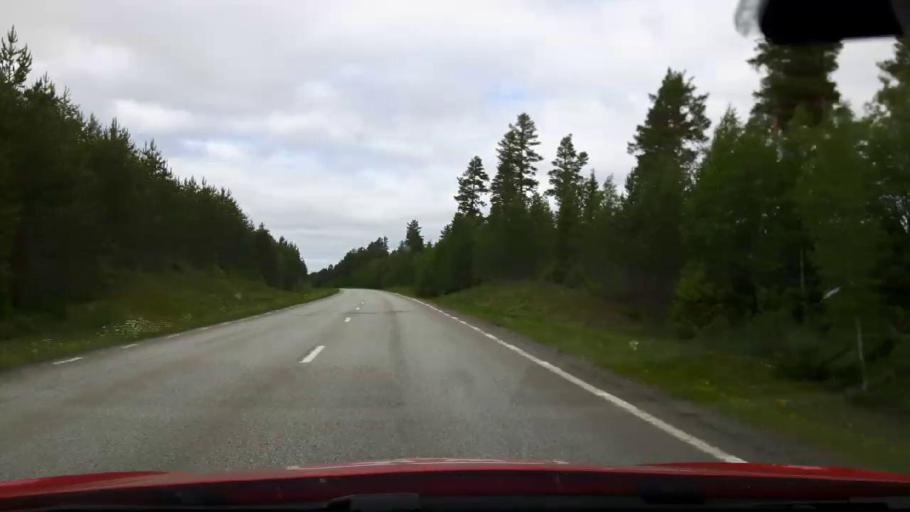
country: SE
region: Jaemtland
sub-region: Krokoms Kommun
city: Krokom
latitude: 63.4348
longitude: 14.4988
